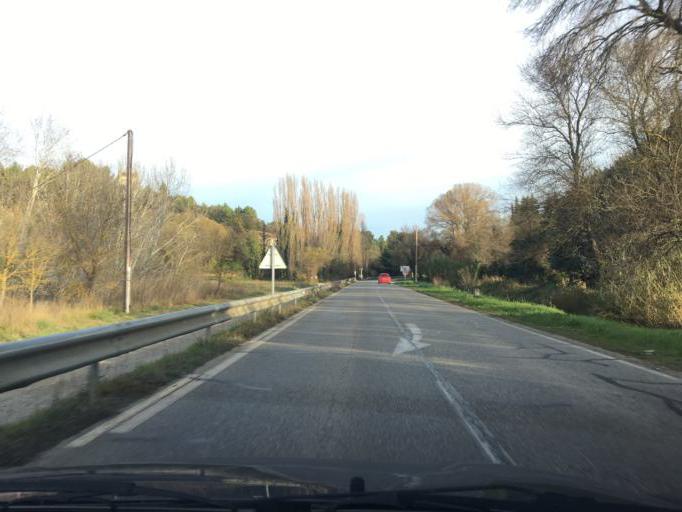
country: FR
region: Provence-Alpes-Cote d'Azur
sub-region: Departement du Vaucluse
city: Lauris
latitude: 43.7399
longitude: 5.3422
